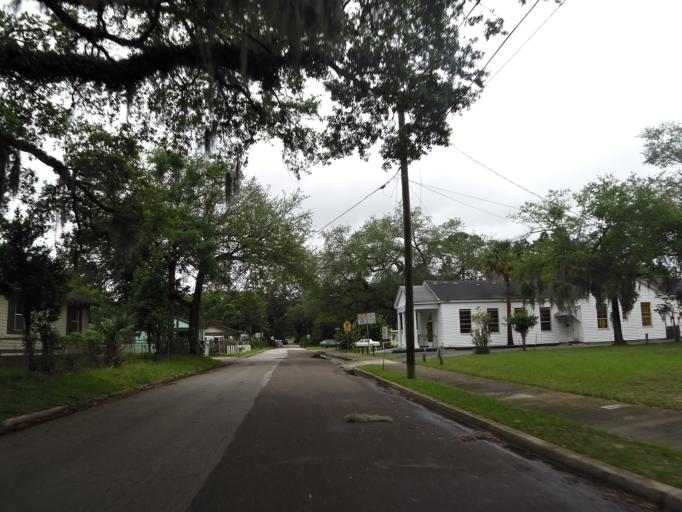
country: US
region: Florida
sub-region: Duval County
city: Jacksonville
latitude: 30.3463
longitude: -81.6324
